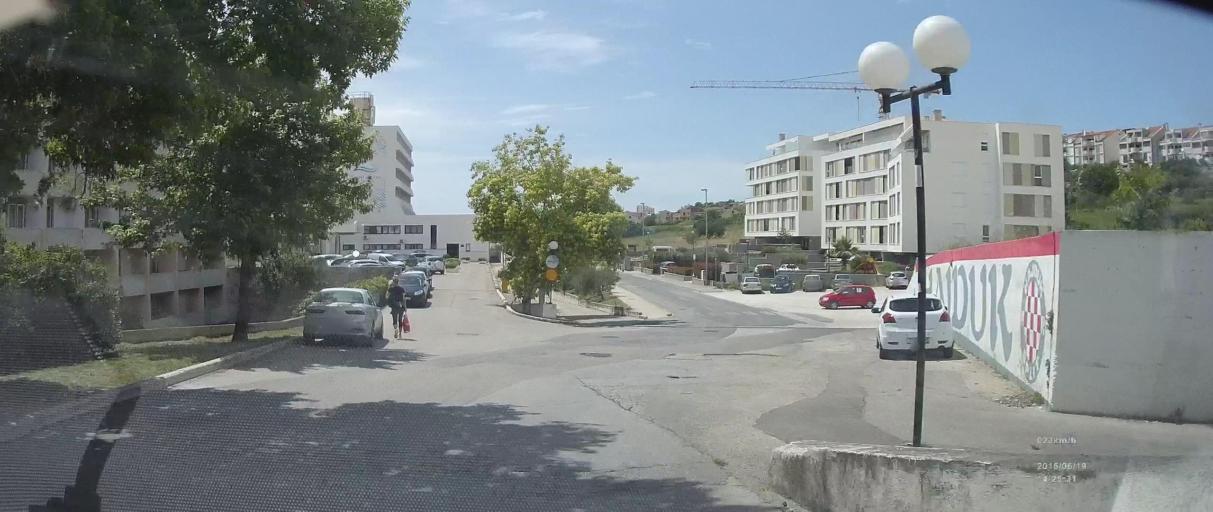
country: HR
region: Splitsko-Dalmatinska
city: Kamen
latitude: 43.5037
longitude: 16.4945
